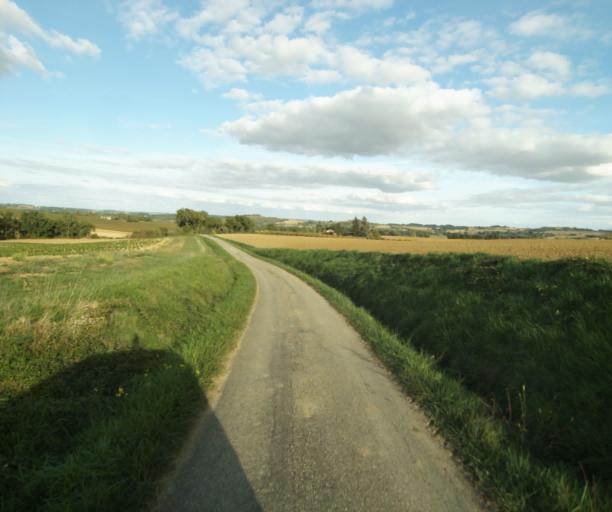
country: FR
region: Midi-Pyrenees
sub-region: Departement du Gers
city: Gondrin
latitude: 43.8968
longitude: 0.2707
